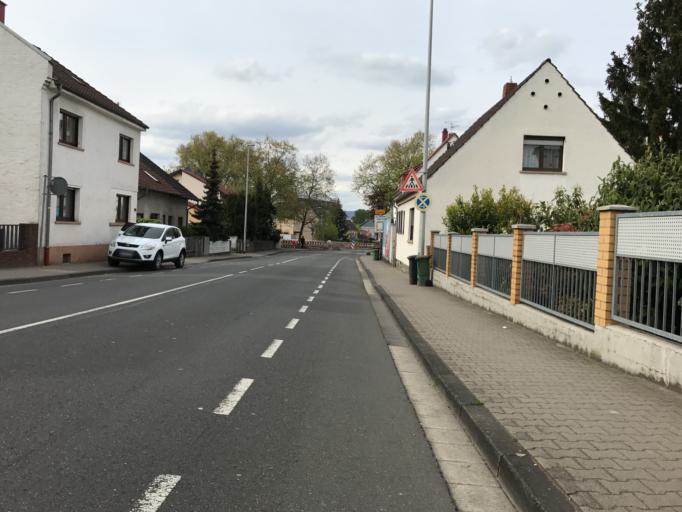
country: DE
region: Rheinland-Pfalz
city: Budenheim
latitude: 50.0218
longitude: 8.2205
